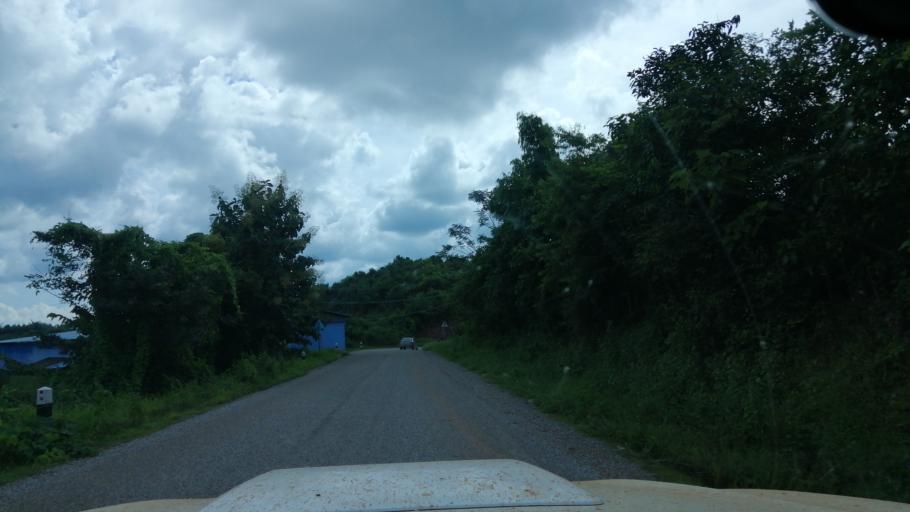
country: TH
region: Uttaradit
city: Ban Khok
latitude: 18.3760
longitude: 101.1504
